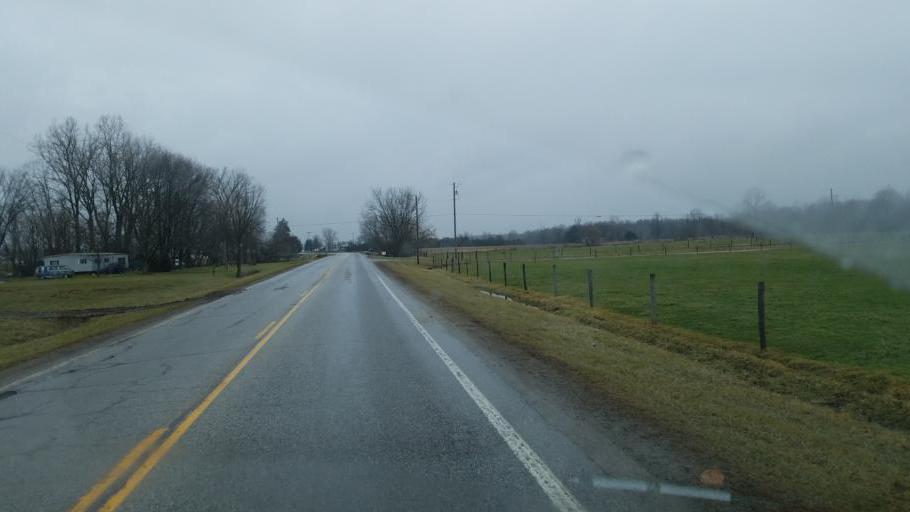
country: US
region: Ohio
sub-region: Geauga County
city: Middlefield
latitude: 41.4206
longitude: -80.9550
